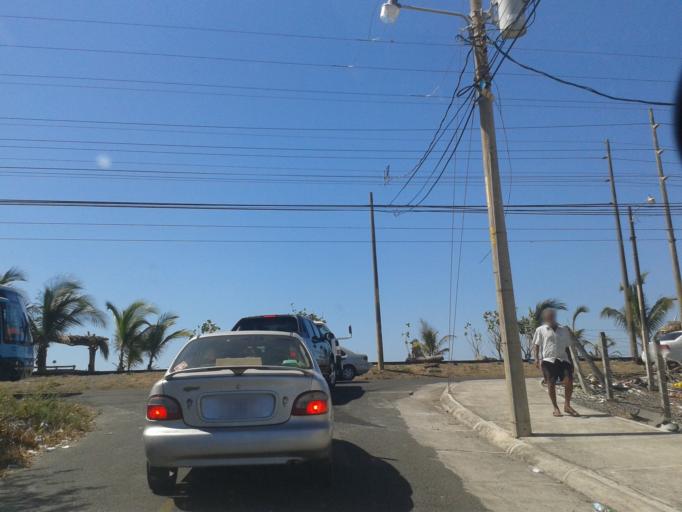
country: CR
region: Puntarenas
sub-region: Canton Central de Puntarenas
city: Chacarita
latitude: 9.9809
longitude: -84.7990
